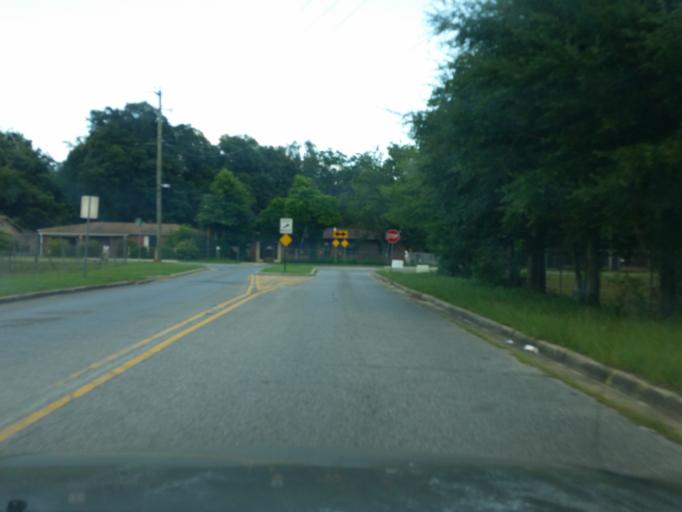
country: US
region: Florida
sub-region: Escambia County
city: Ferry Pass
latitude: 30.5078
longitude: -87.2181
